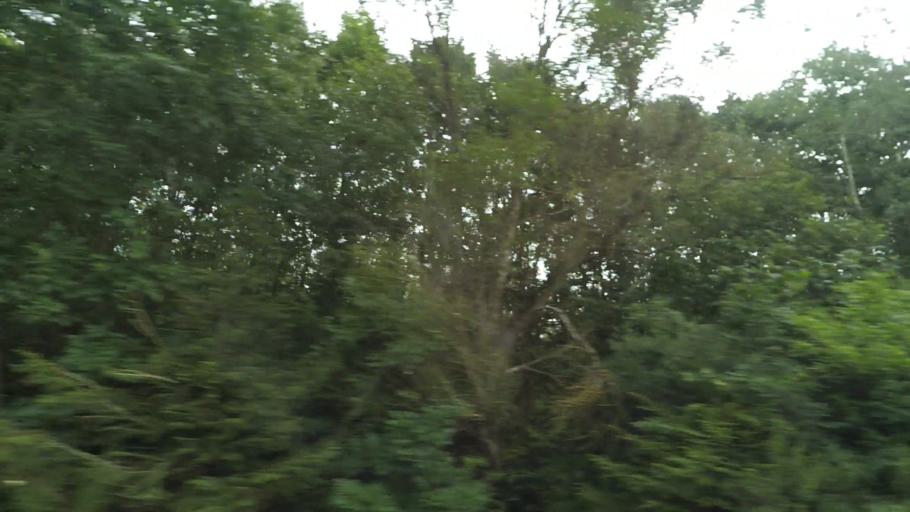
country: DK
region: Central Jutland
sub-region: Syddjurs Kommune
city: Ryomgard
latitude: 56.4155
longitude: 10.5619
